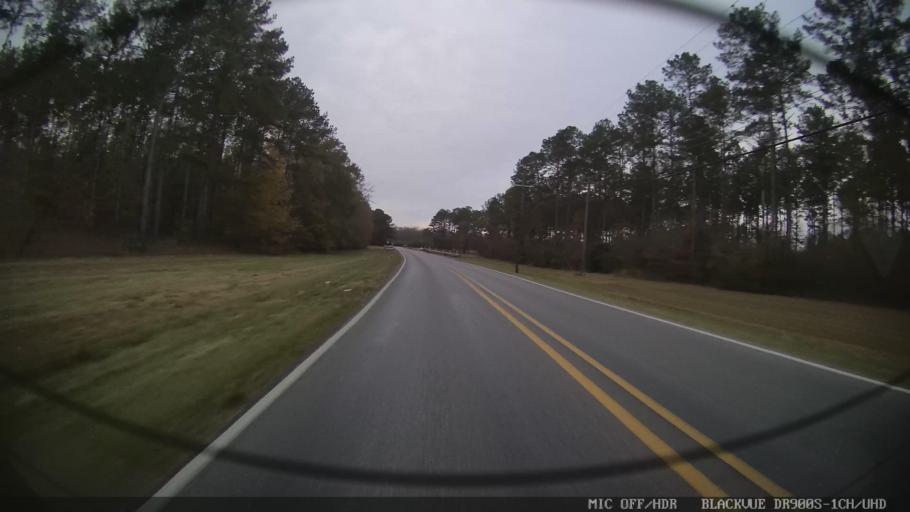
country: US
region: Mississippi
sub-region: Clarke County
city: Quitman
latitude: 32.0430
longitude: -88.7495
